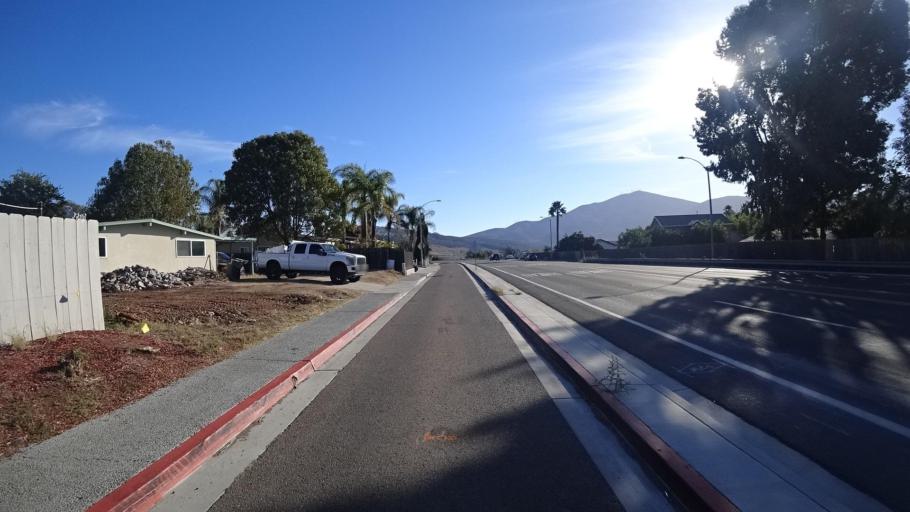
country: US
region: California
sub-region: San Diego County
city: La Presa
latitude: 32.7087
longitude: -116.9858
